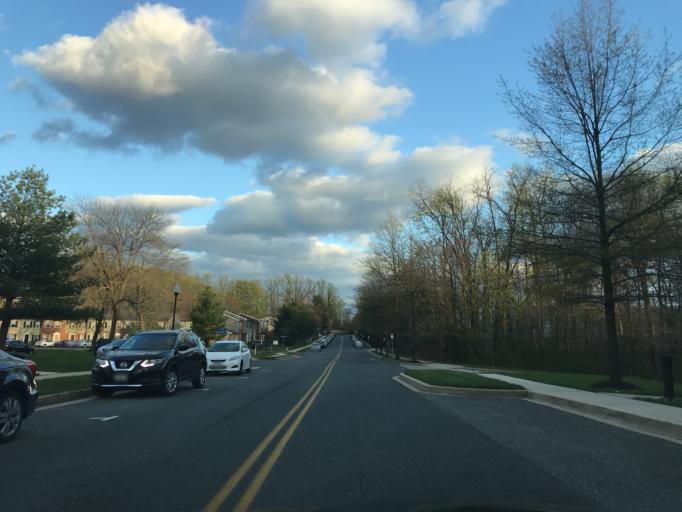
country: US
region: Maryland
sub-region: Harford County
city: Bel Air
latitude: 39.5254
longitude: -76.3469
